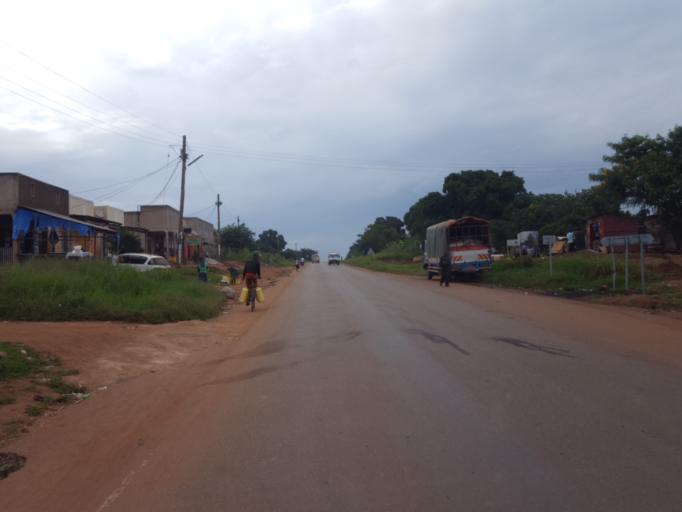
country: UG
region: Central Region
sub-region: Kyankwanzi District
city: Kyankwanzi
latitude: 1.1246
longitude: 31.5967
